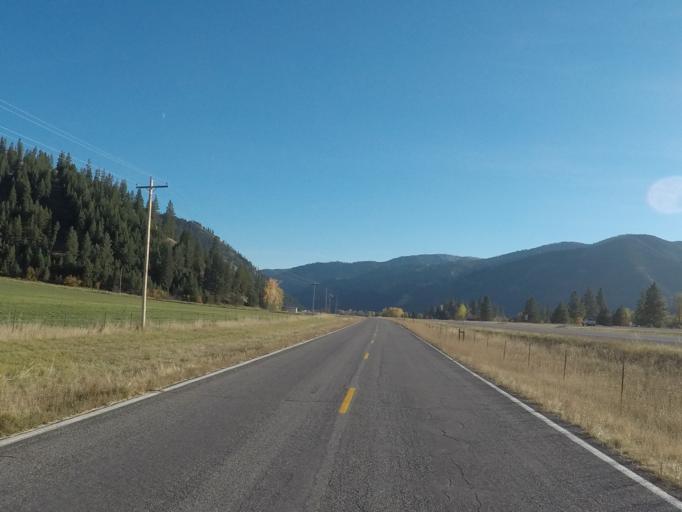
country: US
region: Montana
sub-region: Missoula County
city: Clinton
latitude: 46.7705
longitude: -113.7104
